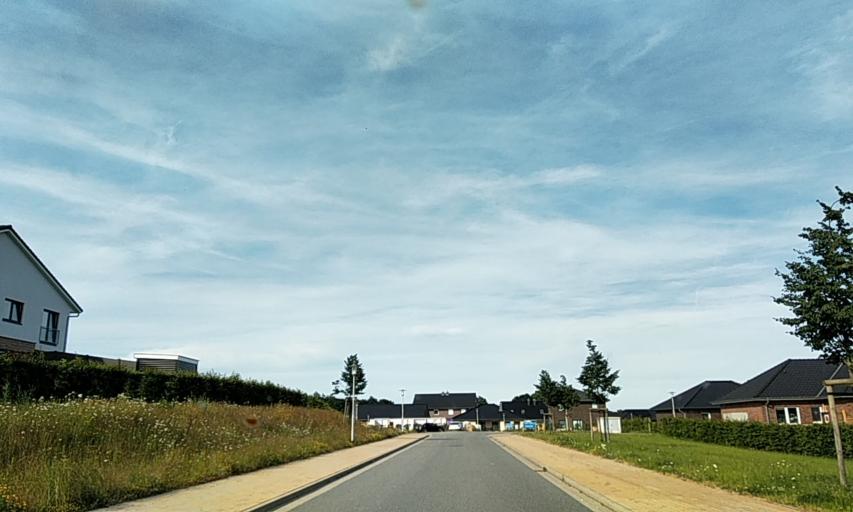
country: DE
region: Schleswig-Holstein
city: Schleswig
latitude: 54.5368
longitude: 9.5655
